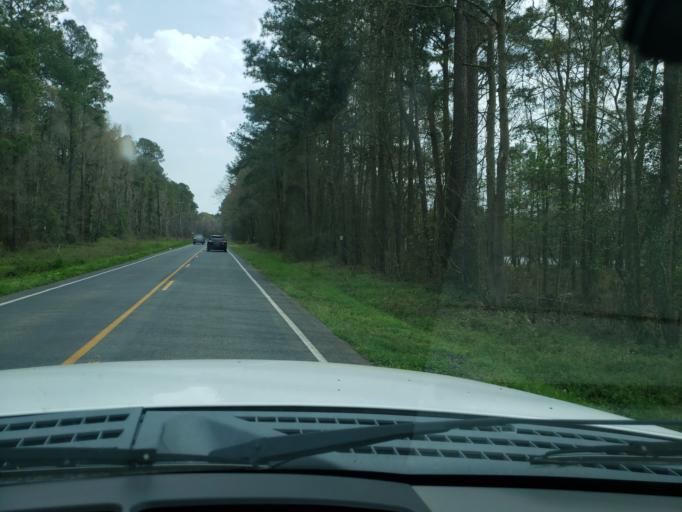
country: US
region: North Carolina
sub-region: Duplin County
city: Beulaville
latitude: 34.7897
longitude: -77.8445
